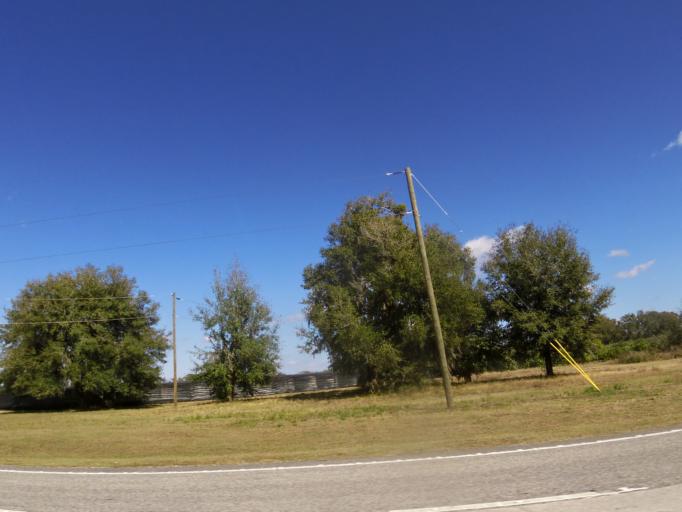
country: US
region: Florida
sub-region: Volusia County
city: Pierson
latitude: 29.2072
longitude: -81.4463
